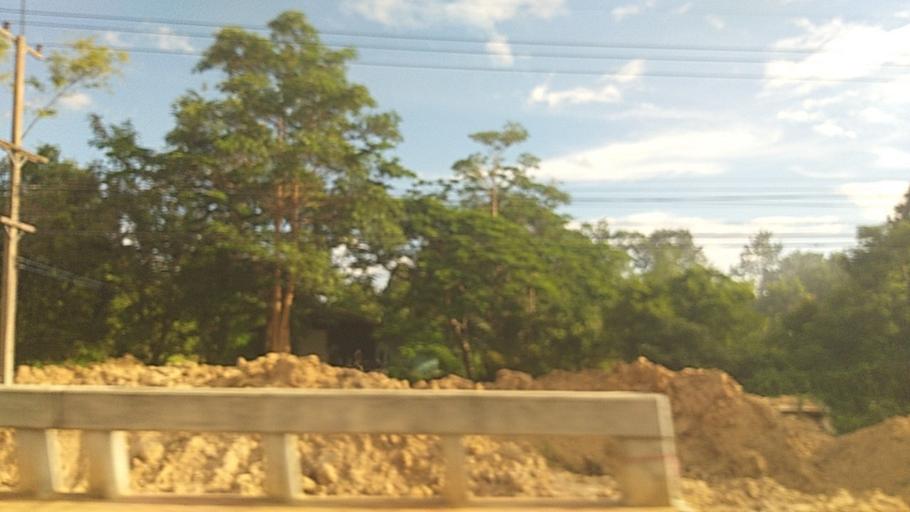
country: TH
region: Surin
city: Kap Choeng
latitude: 14.4726
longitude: 103.6080
